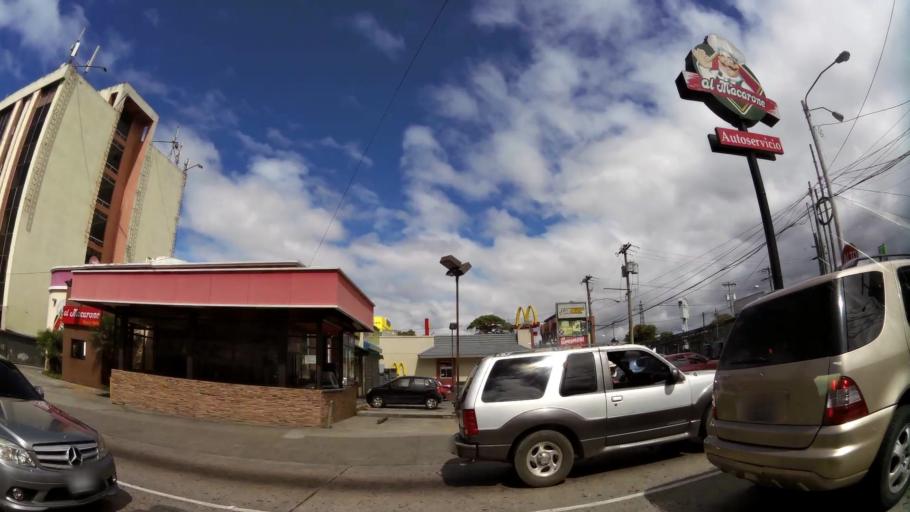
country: GT
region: Guatemala
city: Guatemala City
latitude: 14.6093
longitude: -90.5193
